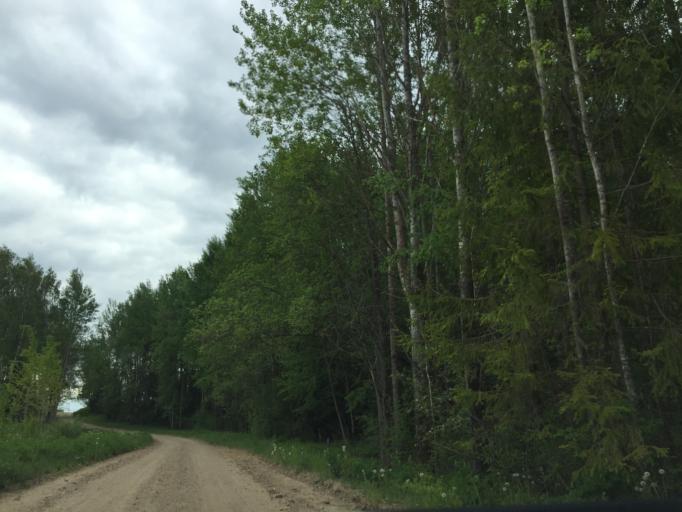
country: LV
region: Aglona
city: Aglona
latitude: 56.1758
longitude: 27.2515
